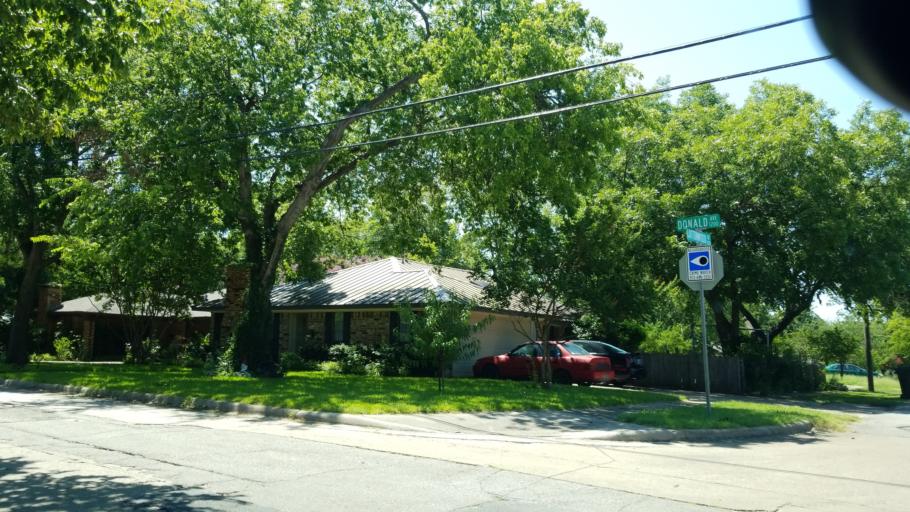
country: US
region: Texas
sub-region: Dallas County
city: Carrollton
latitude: 32.9627
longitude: -96.9109
